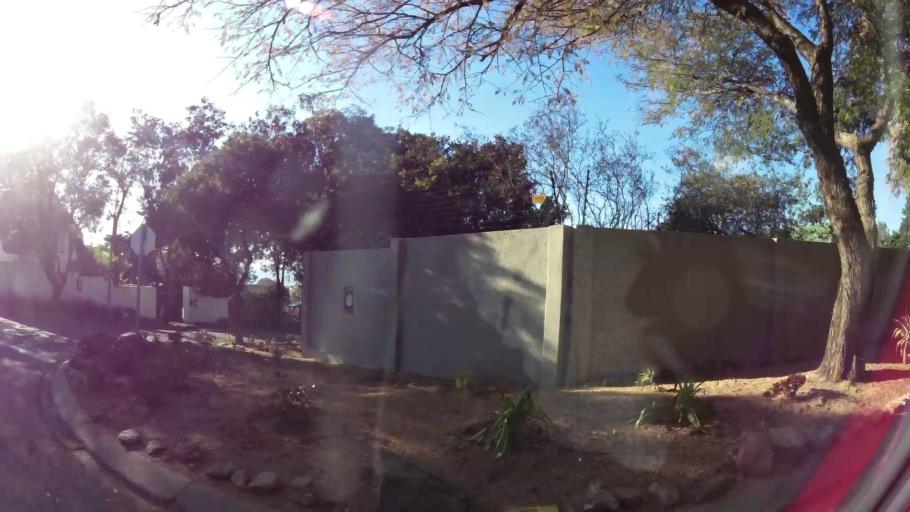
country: ZA
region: Gauteng
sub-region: City of Johannesburg Metropolitan Municipality
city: Midrand
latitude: -26.0315
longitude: 28.0434
